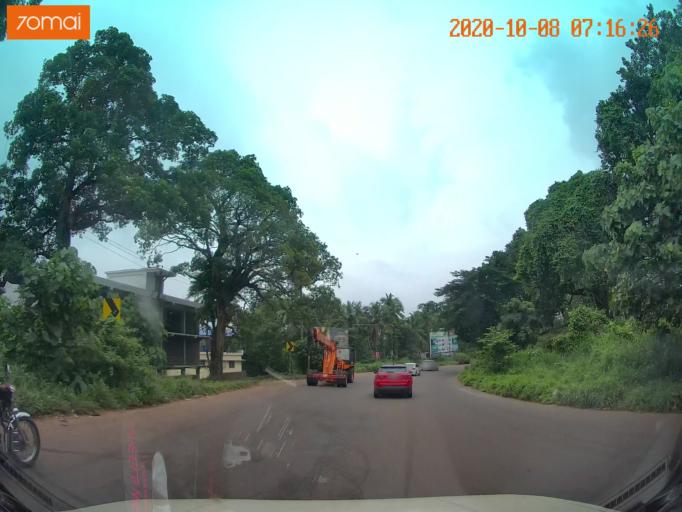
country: IN
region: Kerala
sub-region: Malappuram
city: Ponnani
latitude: 10.8311
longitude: 76.0201
